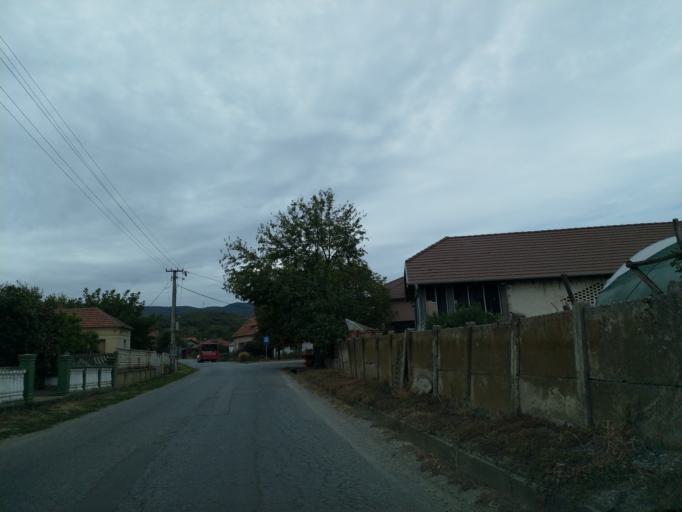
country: RS
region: Central Serbia
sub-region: Pomoravski Okrug
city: Paracin
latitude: 43.8351
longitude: 21.3270
